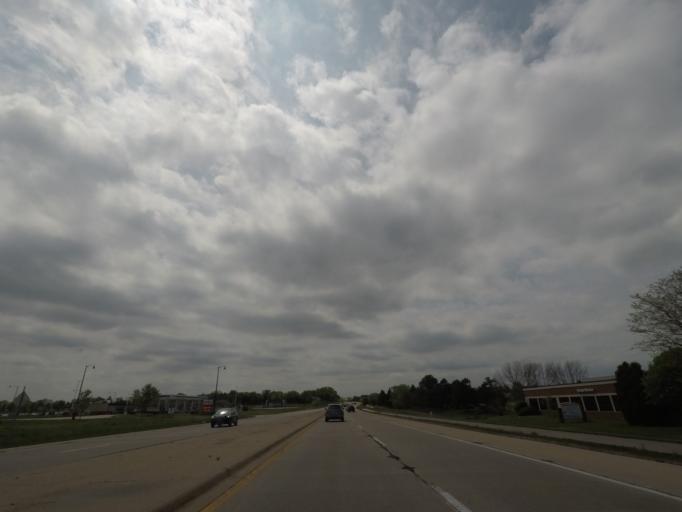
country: US
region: Illinois
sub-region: Winnebago County
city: Cherry Valley
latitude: 42.2947
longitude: -88.9801
